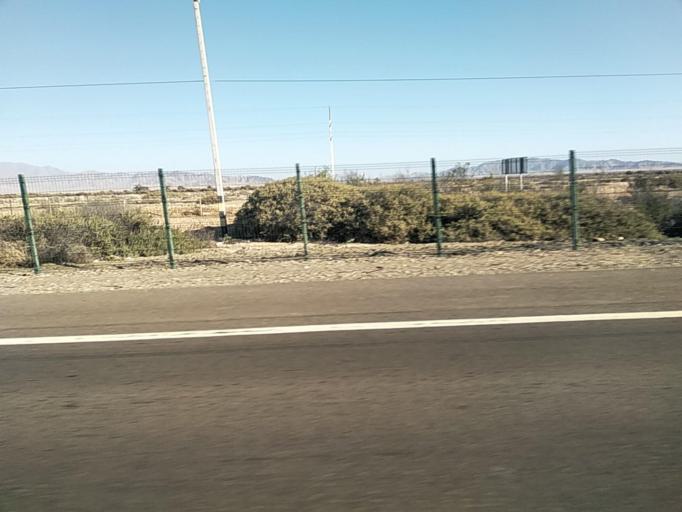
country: CL
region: Atacama
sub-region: Provincia de Copiapo
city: Copiapo
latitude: -27.3555
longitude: -70.6633
